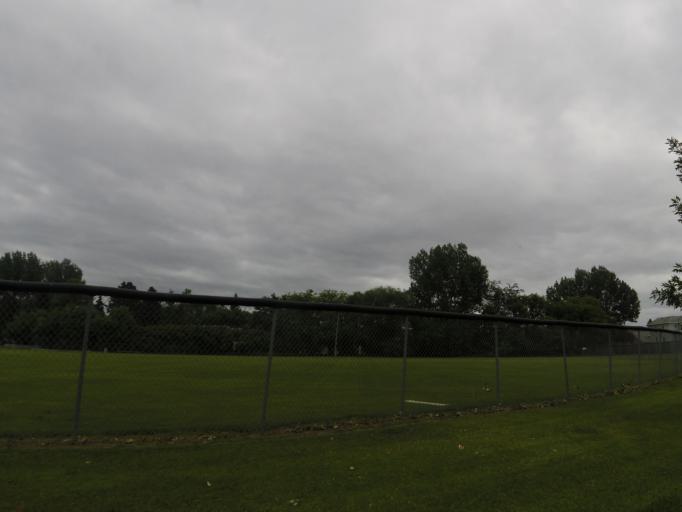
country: US
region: North Dakota
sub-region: Walsh County
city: Grafton
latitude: 48.6201
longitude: -97.4539
